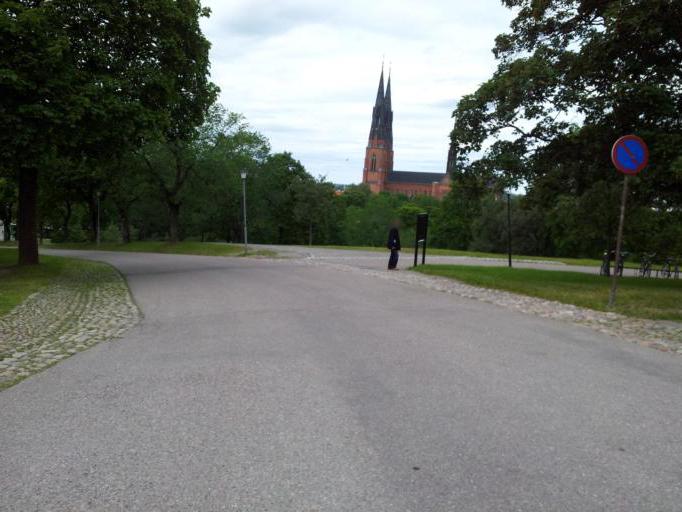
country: SE
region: Uppsala
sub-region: Uppsala Kommun
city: Uppsala
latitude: 59.8542
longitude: 17.6345
